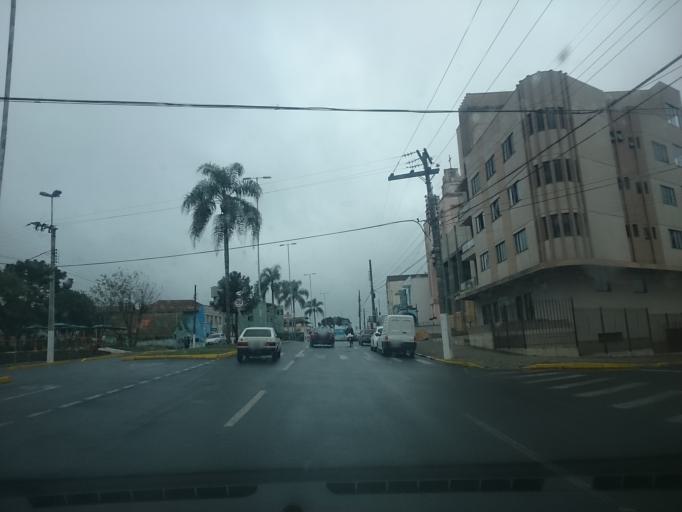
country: BR
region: Santa Catarina
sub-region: Lages
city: Lages
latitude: -27.8199
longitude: -50.3325
